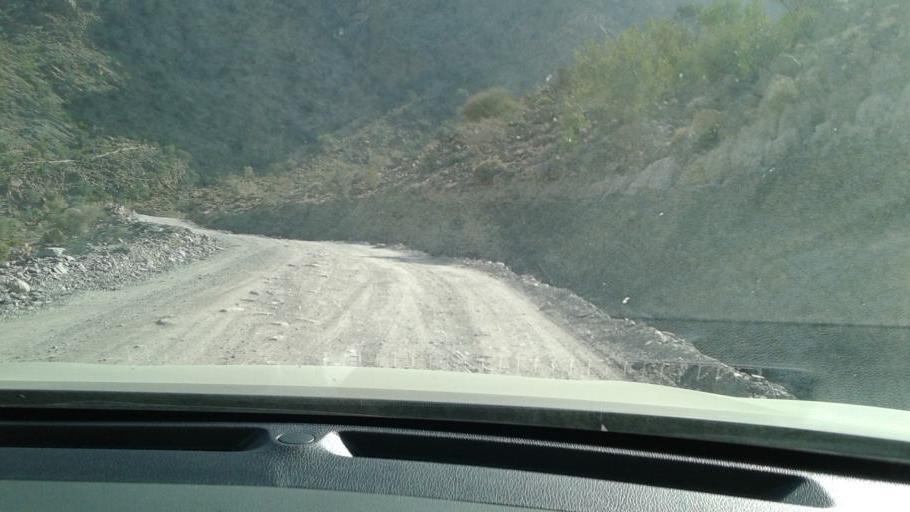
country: OM
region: Al Batinah
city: Bayt al `Awabi
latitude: 23.1802
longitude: 57.4074
